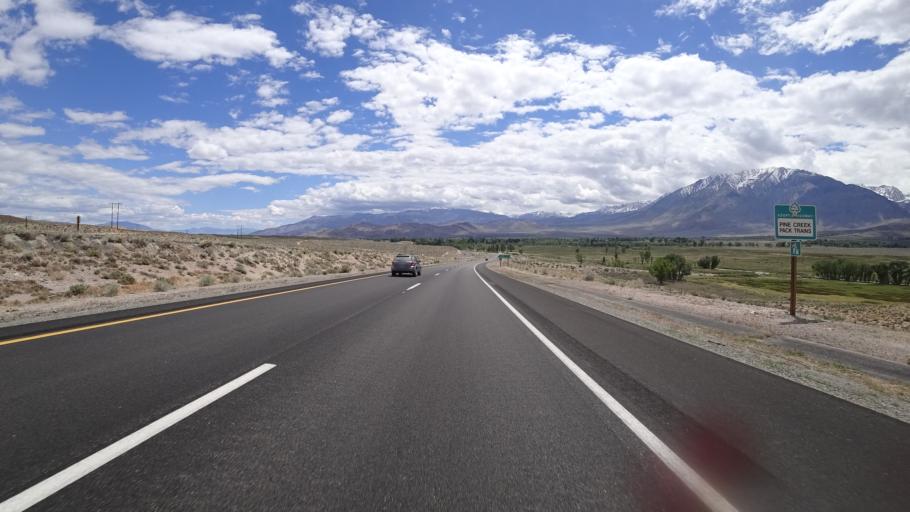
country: US
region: California
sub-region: Inyo County
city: West Bishop
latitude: 37.4492
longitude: -118.5728
